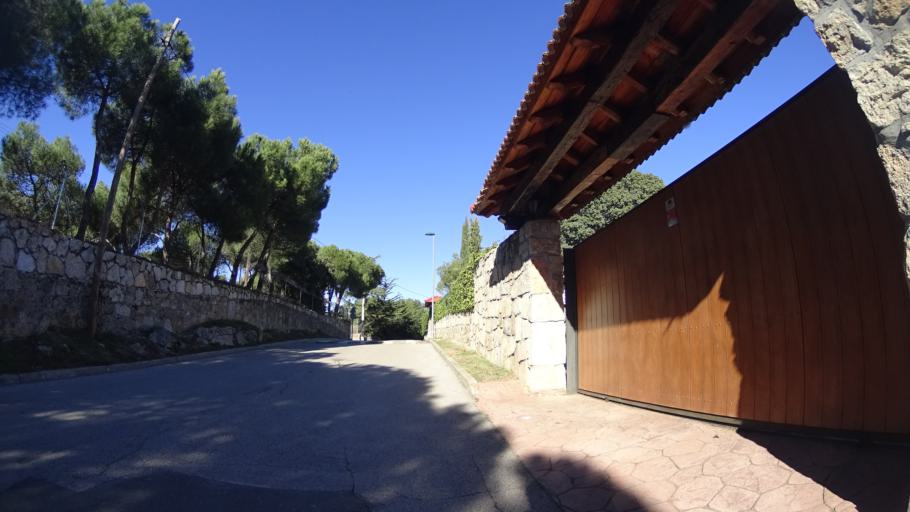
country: ES
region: Madrid
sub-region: Provincia de Madrid
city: Torrelodones
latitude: 40.5888
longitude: -3.9520
